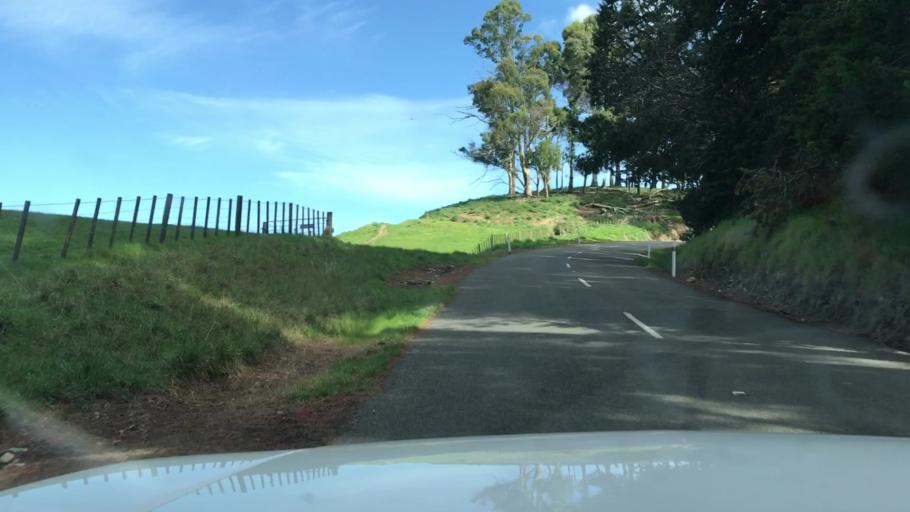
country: NZ
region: Hawke's Bay
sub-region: Hastings District
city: Hastings
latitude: -39.8145
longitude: 176.7517
